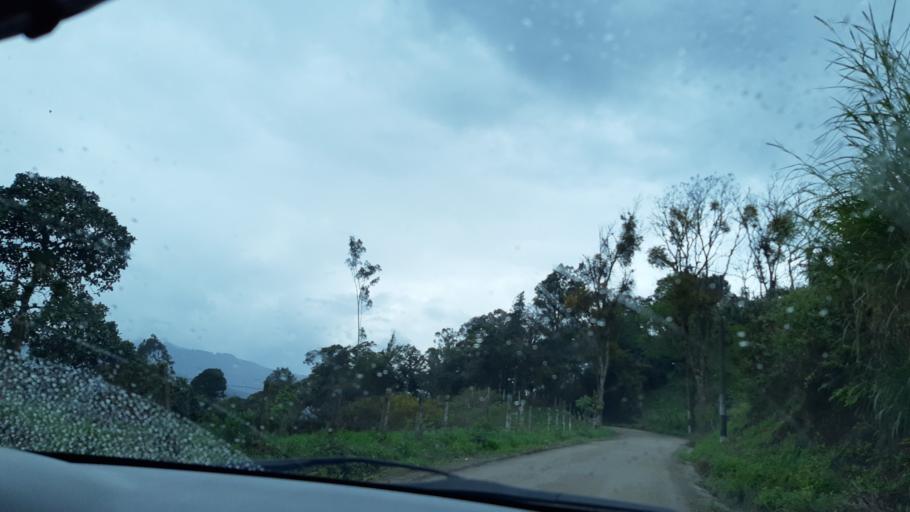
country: CO
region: Boyaca
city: Chivor
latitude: 4.9706
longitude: -73.3187
